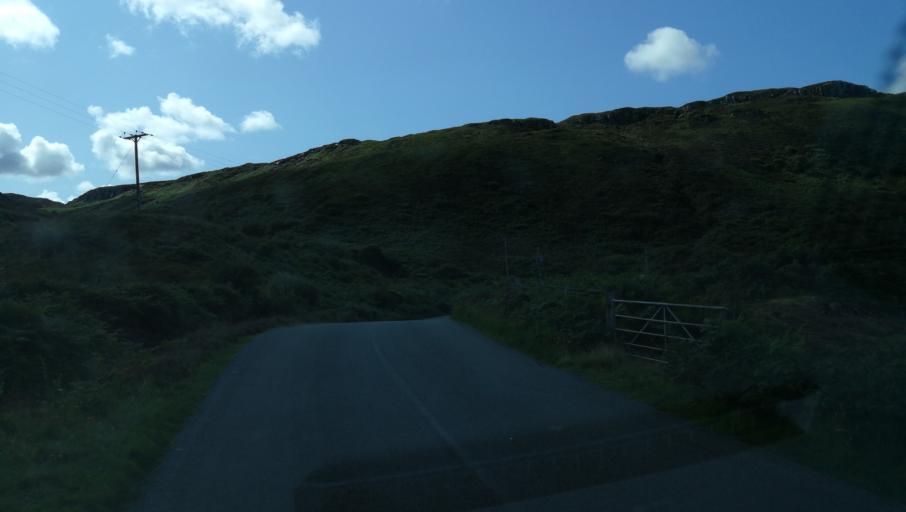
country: GB
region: Scotland
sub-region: Highland
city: Isle of Skye
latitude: 57.4513
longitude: -6.6631
